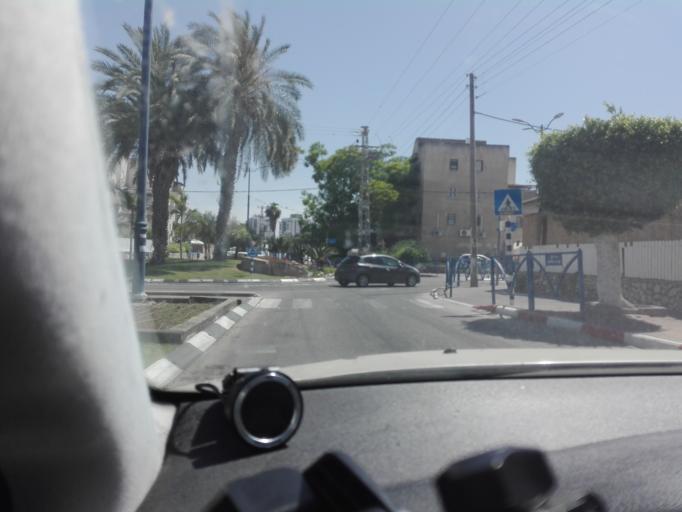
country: IL
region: Central District
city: Bene 'Ayish
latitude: 31.7313
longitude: 34.7399
